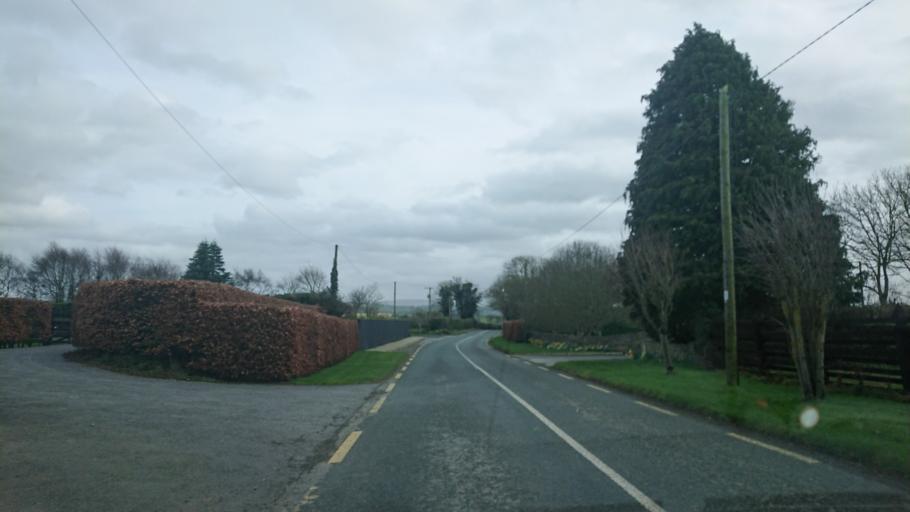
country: IE
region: Leinster
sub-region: Kildare
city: Naas
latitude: 53.1911
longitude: -6.6461
